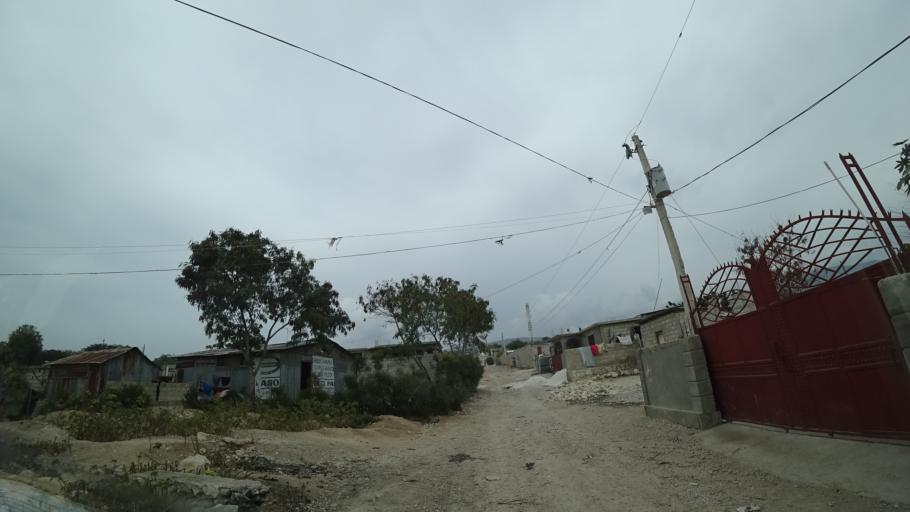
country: HT
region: Ouest
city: Croix des Bouquets
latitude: 18.6537
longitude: -72.2659
